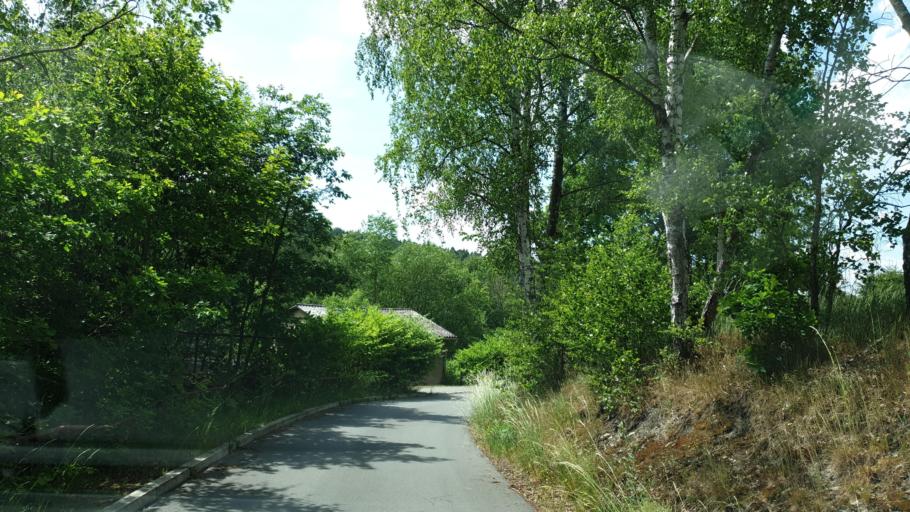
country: DE
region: Saxony
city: Adorf
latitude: 50.3346
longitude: 12.2573
